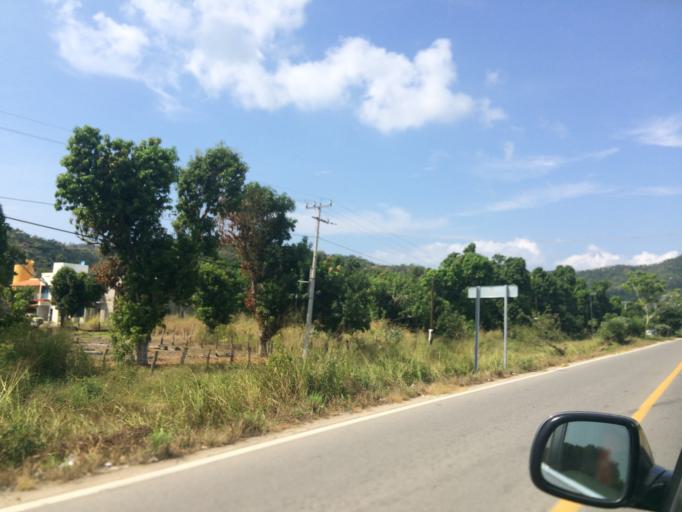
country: MX
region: Jalisco
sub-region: Cihuatlan
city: Emiliano Zapata (El Ranchito)
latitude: 19.2389
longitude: -104.7111
